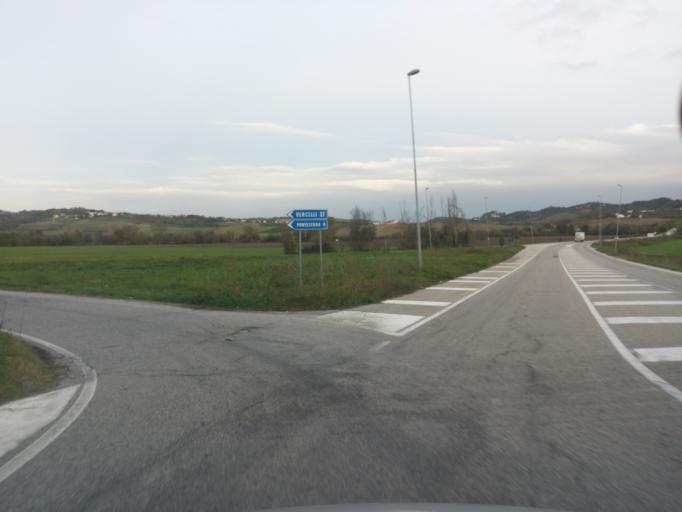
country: IT
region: Piedmont
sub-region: Provincia di Alessandria
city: Cereseto
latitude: 45.1126
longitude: 8.3240
